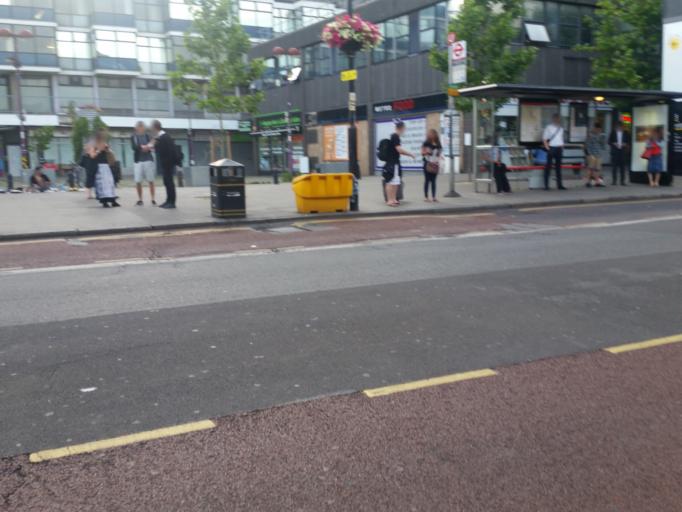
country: GB
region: England
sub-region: Greater London
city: Holloway
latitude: 51.5647
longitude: -0.1350
